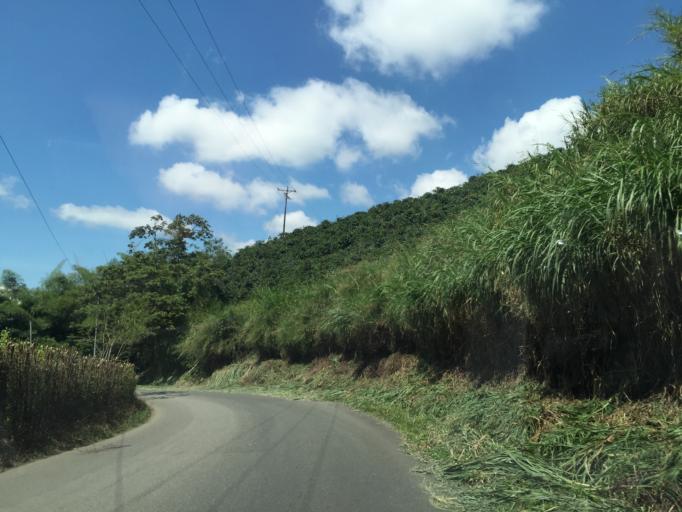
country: CO
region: Valle del Cauca
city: Alcala
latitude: 4.7013
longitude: -75.7939
